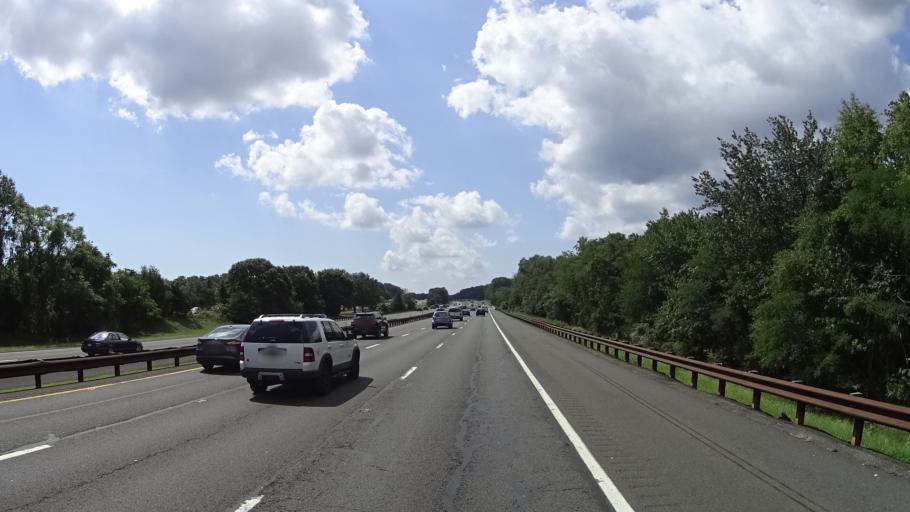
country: US
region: New Jersey
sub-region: Monmouth County
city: Lincroft
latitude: 40.3275
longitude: -74.0989
